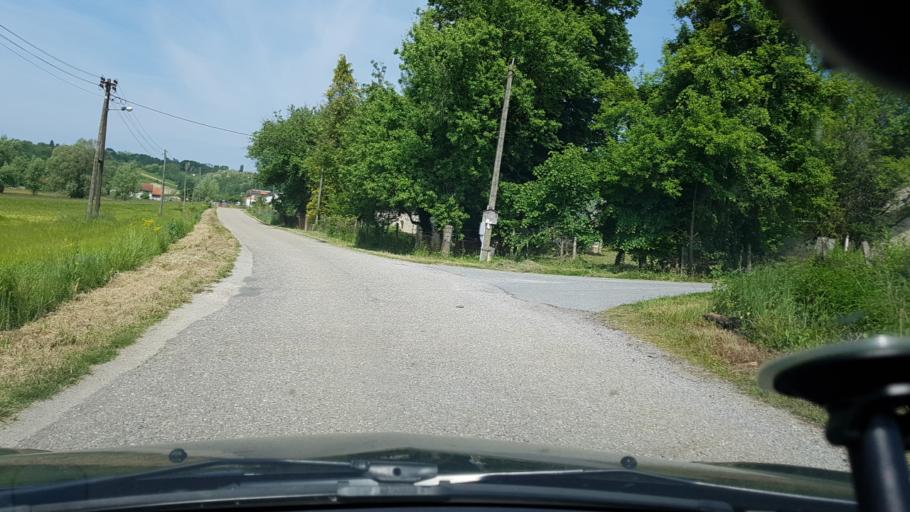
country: HR
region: Krapinsko-Zagorska
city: Selnica
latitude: 46.0207
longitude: 16.0585
